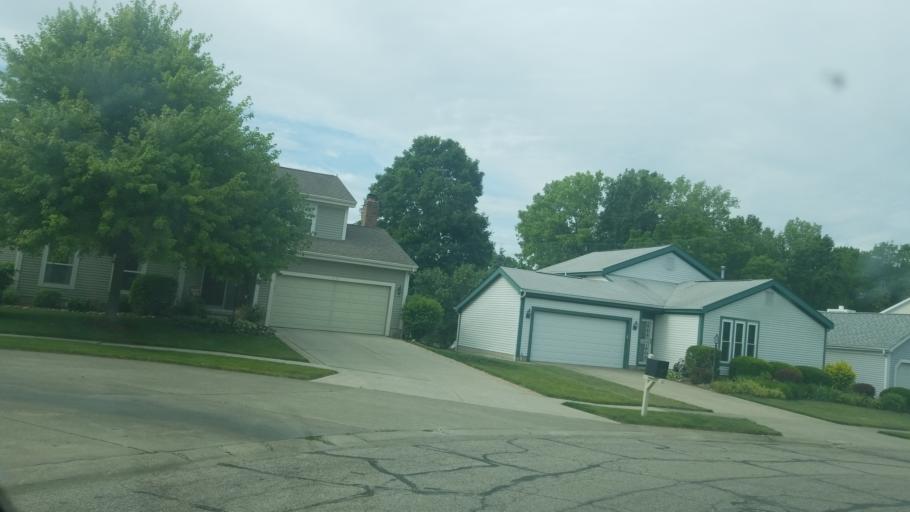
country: US
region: Ohio
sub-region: Franklin County
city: Worthington
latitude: 40.0704
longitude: -83.0016
